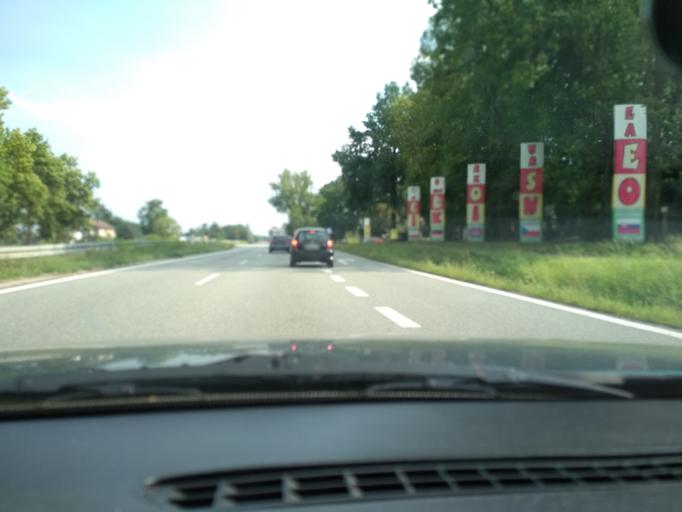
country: PL
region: Silesian Voivodeship
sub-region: Zory
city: Zory
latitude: 50.0118
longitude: 18.7085
